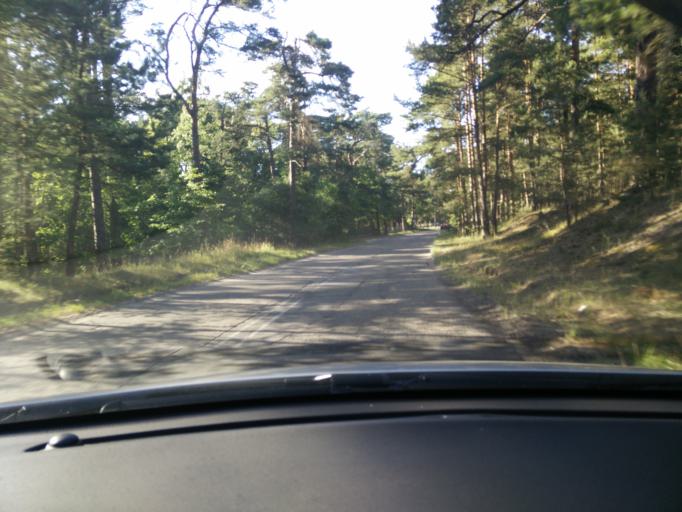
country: PL
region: Pomeranian Voivodeship
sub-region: Powiat pucki
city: Hel
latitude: 54.6515
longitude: 18.7588
